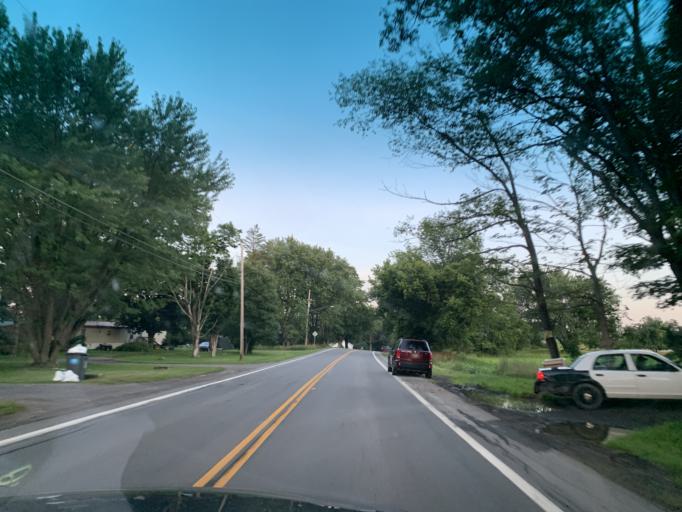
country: US
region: New York
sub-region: Oneida County
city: Waterville
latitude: 42.8731
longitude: -75.2519
